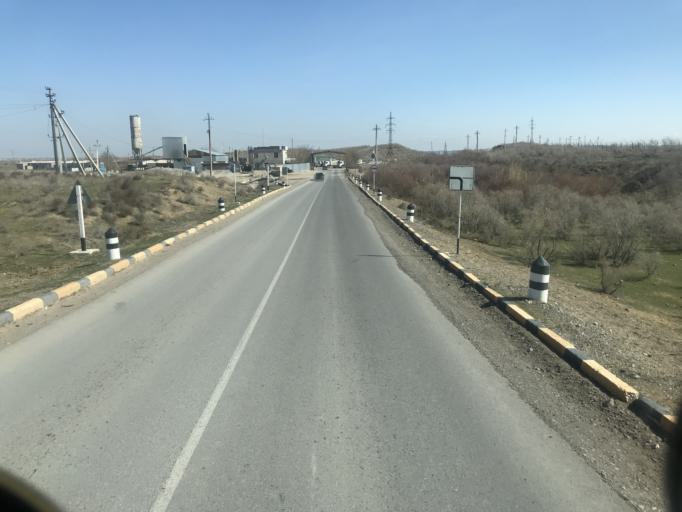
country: KZ
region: Ongtustik Qazaqstan
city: Shardara
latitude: 41.2520
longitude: 67.9068
